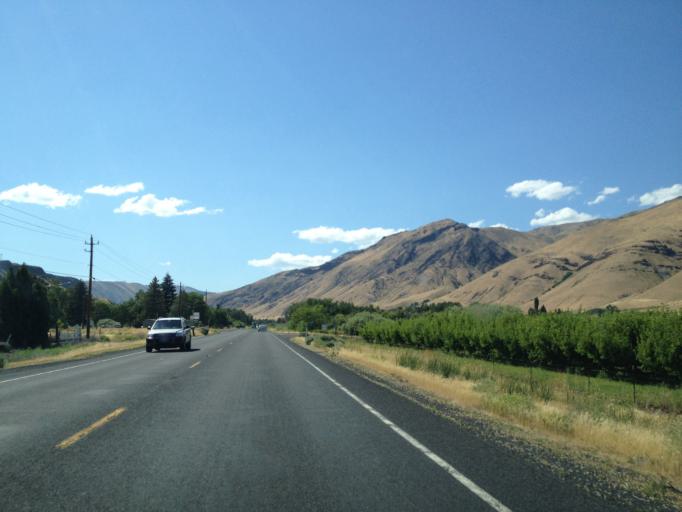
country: US
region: Washington
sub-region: Yakima County
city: Tieton
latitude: 46.7403
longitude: -120.7433
